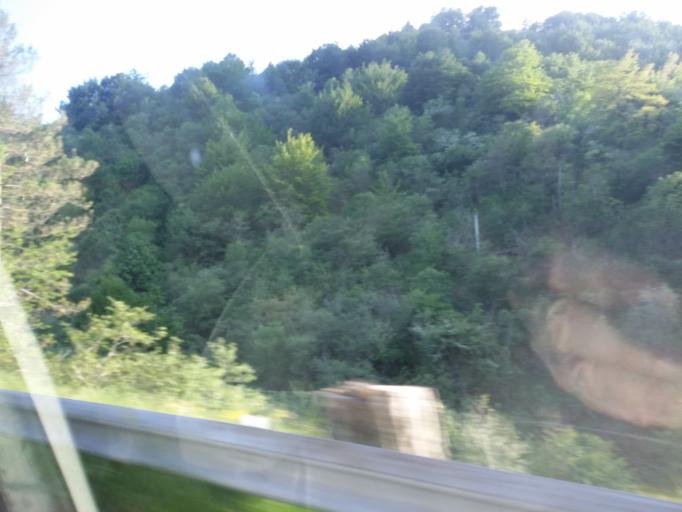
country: IT
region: Liguria
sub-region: Provincia di Genova
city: Lorsica
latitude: 44.4658
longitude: 9.3309
